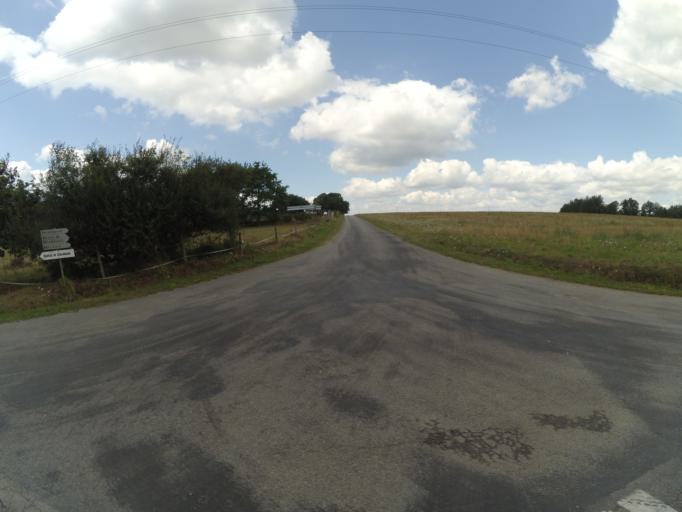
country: FR
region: Brittany
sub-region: Departement du Morbihan
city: Landaul
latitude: 47.7470
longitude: -3.0901
